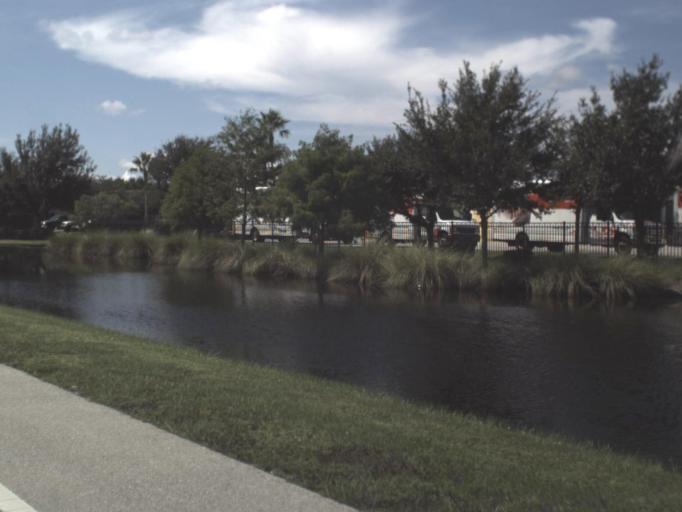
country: US
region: Florida
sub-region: Sarasota County
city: North Port
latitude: 27.0837
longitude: -82.1556
